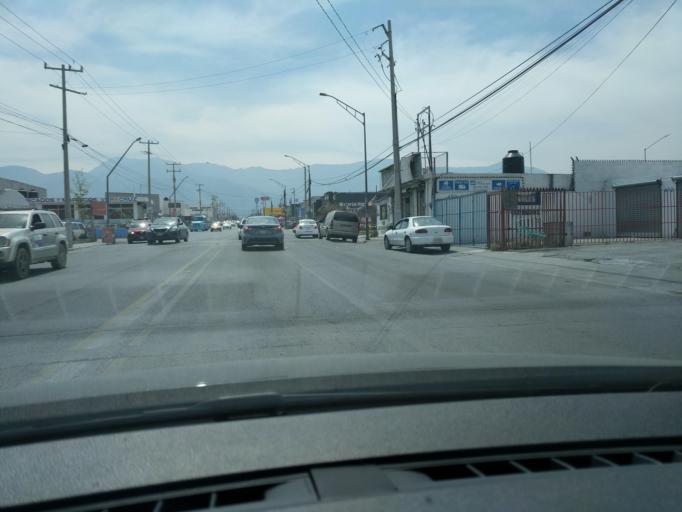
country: MX
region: Coahuila
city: Saltillo
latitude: 25.4274
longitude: -100.9463
